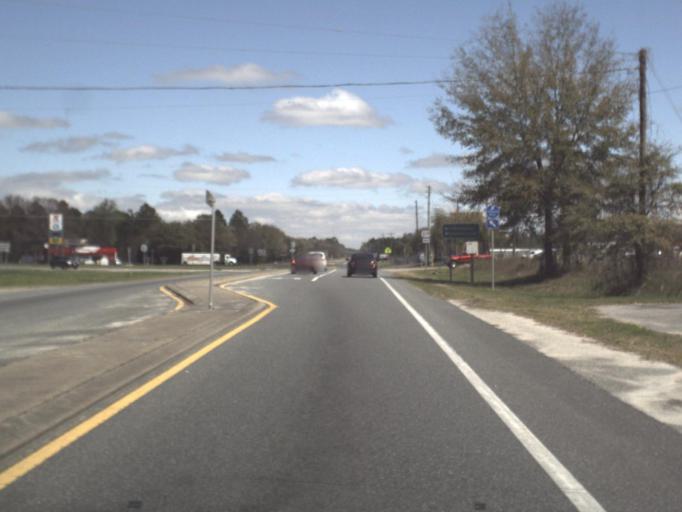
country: US
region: Florida
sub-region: Wakulla County
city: Crawfordville
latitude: 30.1039
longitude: -84.3808
